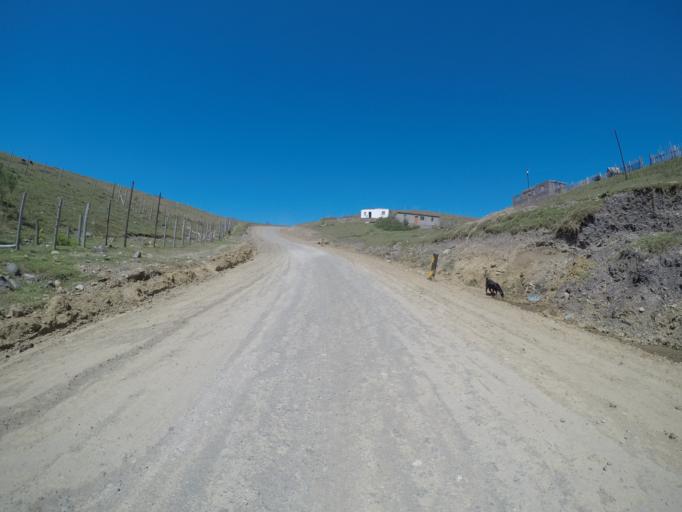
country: ZA
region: Eastern Cape
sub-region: OR Tambo District Municipality
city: Libode
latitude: -31.9894
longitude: 29.1453
